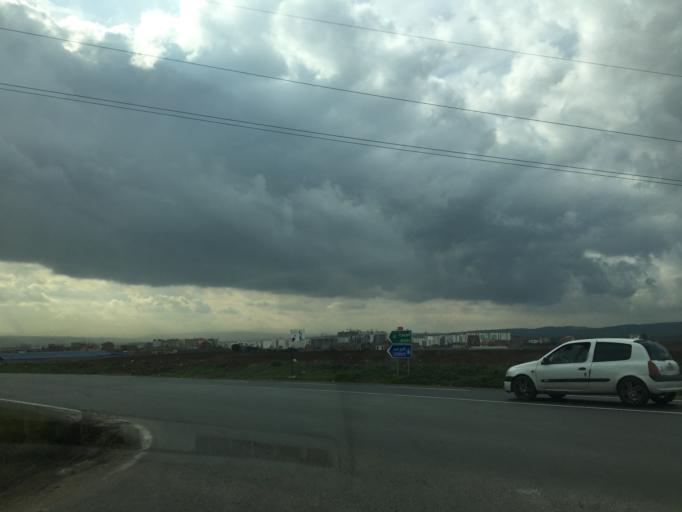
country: DZ
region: Bouira
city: Bouira
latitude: 36.4097
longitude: 3.9057
